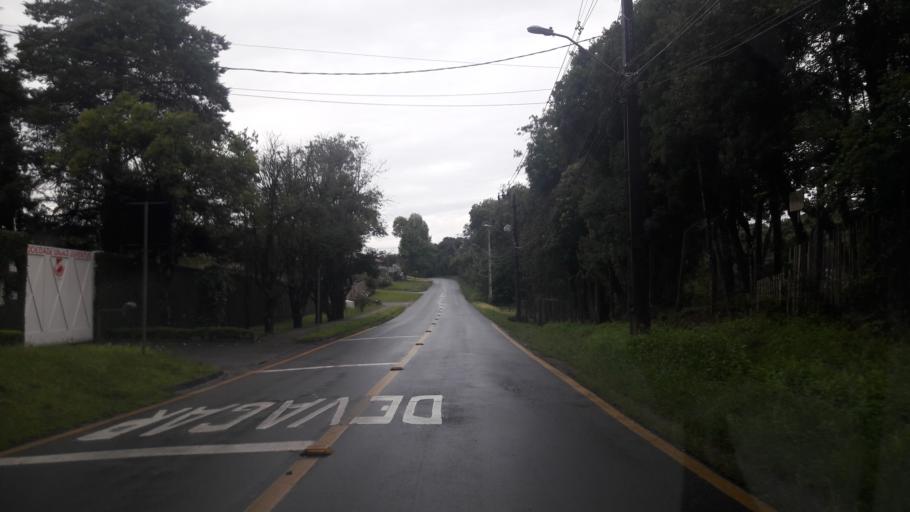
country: BR
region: Parana
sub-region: Curitiba
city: Curitiba
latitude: -25.3937
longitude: -49.3190
